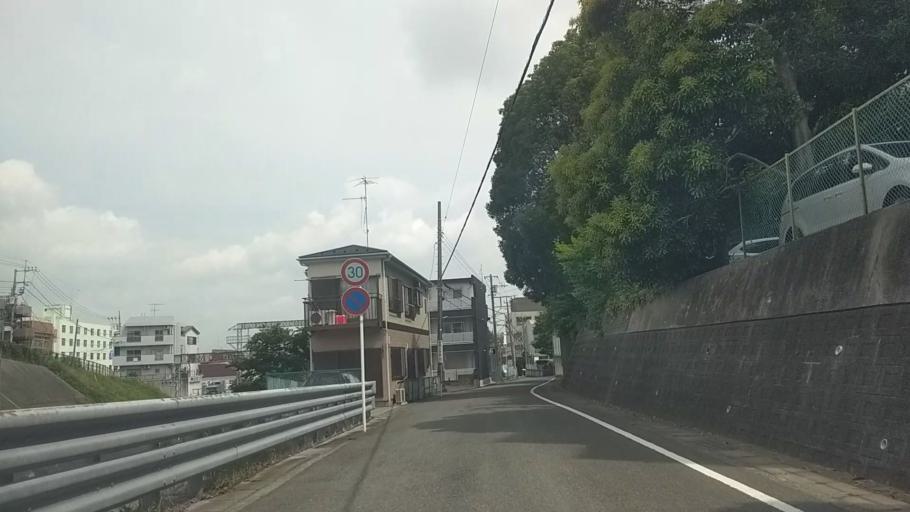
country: JP
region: Kanagawa
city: Fujisawa
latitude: 35.3609
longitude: 139.4738
